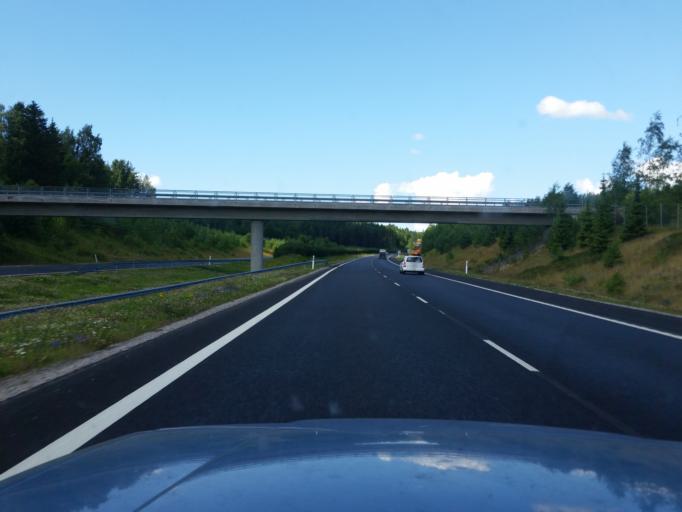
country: FI
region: Varsinais-Suomi
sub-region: Salo
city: Muurla
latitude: 60.3905
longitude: 23.2805
